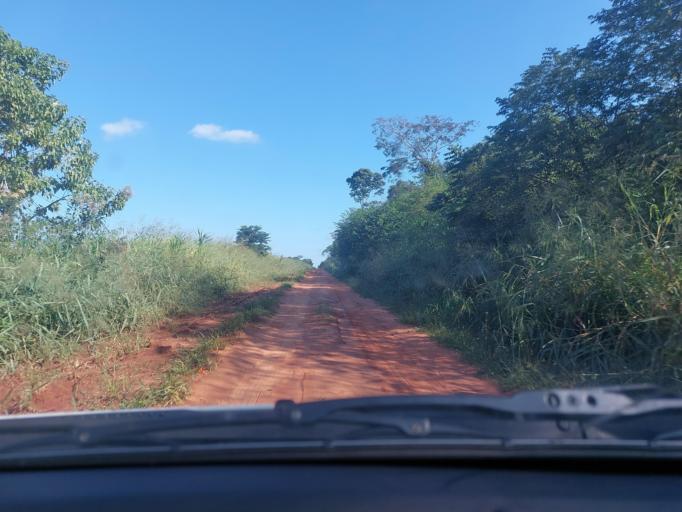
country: PY
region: San Pedro
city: Guayaybi
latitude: -24.5057
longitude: -56.5460
